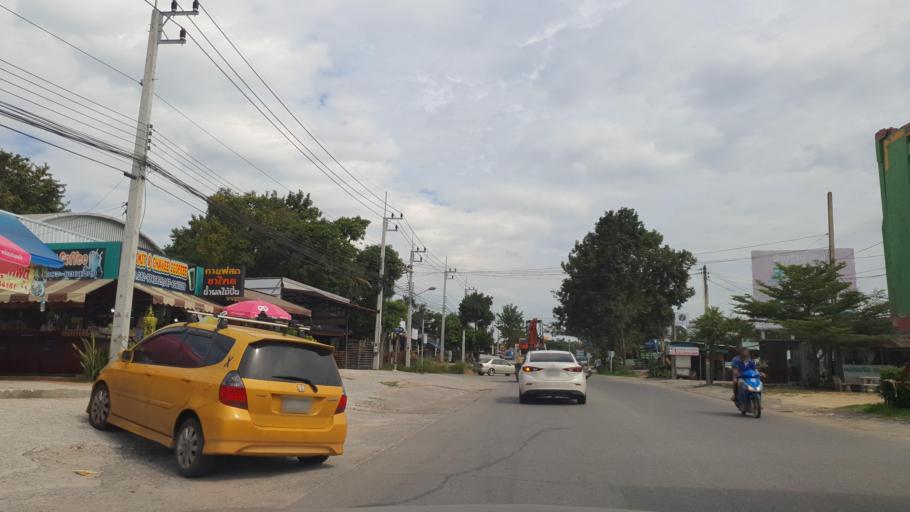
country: TH
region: Chon Buri
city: Phatthaya
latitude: 12.9430
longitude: 100.9461
